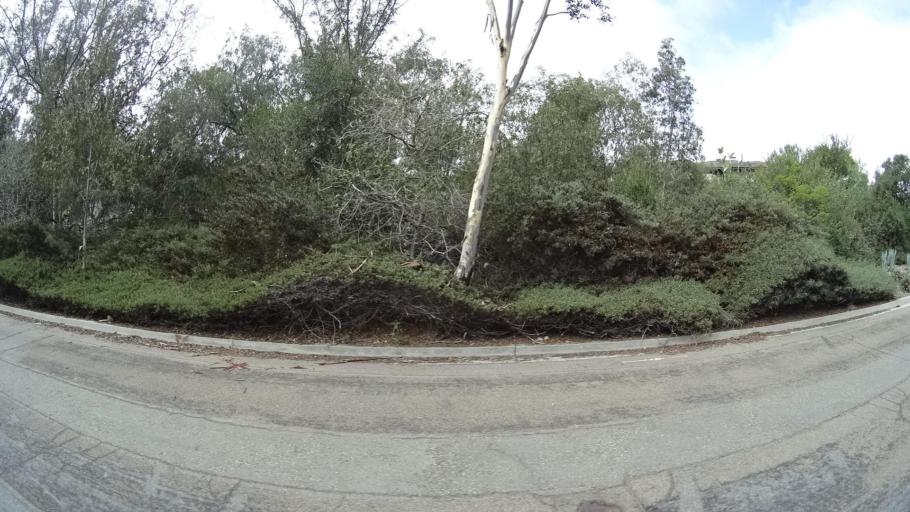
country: US
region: California
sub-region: San Diego County
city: Rancho Santa Fe
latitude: 33.0096
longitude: -117.2216
